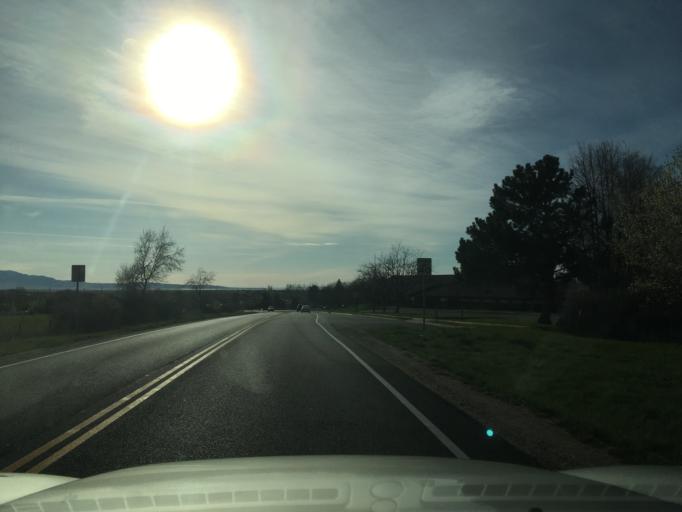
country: US
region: Utah
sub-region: Davis County
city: Kaysville
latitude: 41.0625
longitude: -111.9370
